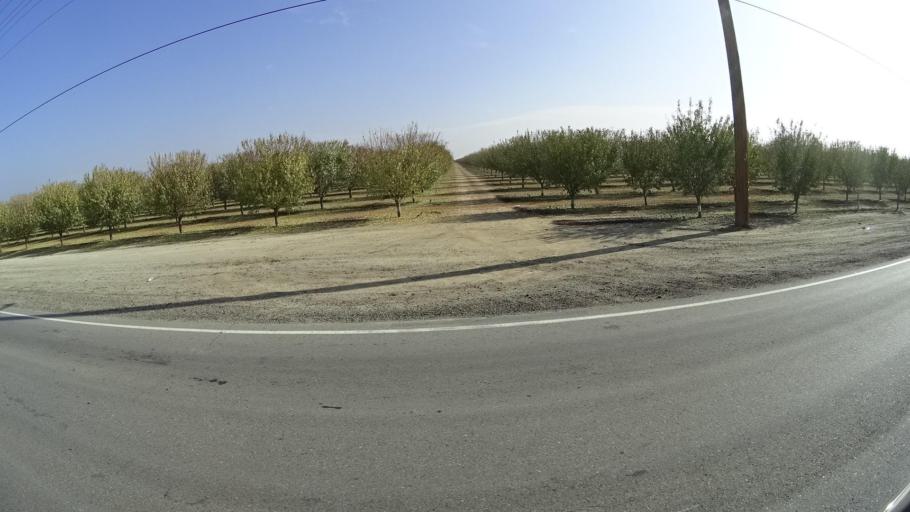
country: US
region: California
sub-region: Kern County
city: McFarland
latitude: 35.7218
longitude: -119.2231
